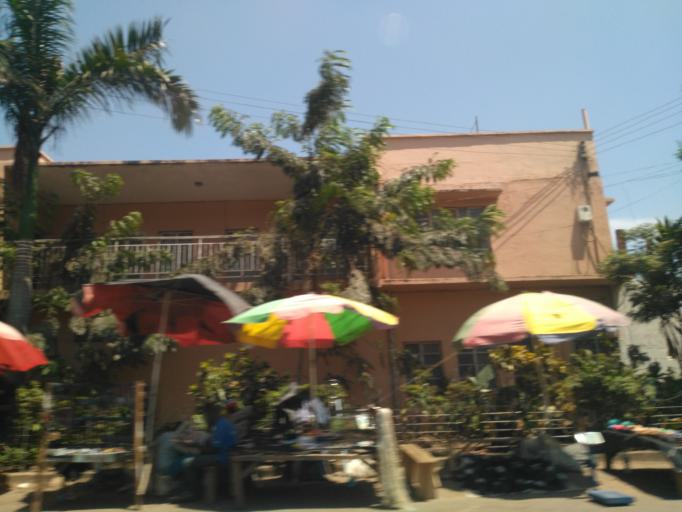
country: TZ
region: Mwanza
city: Mwanza
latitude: -2.5228
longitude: 32.9034
